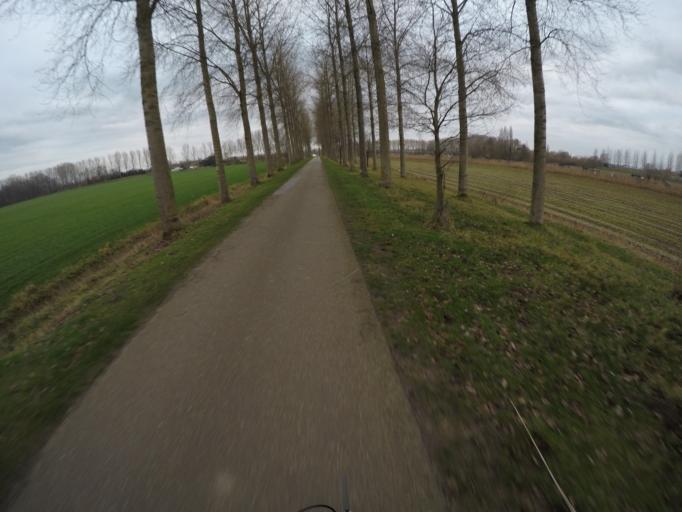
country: BE
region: Flanders
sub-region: Provincie Oost-Vlaanderen
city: Sint-Gillis-Waas
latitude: 51.2437
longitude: 4.1294
